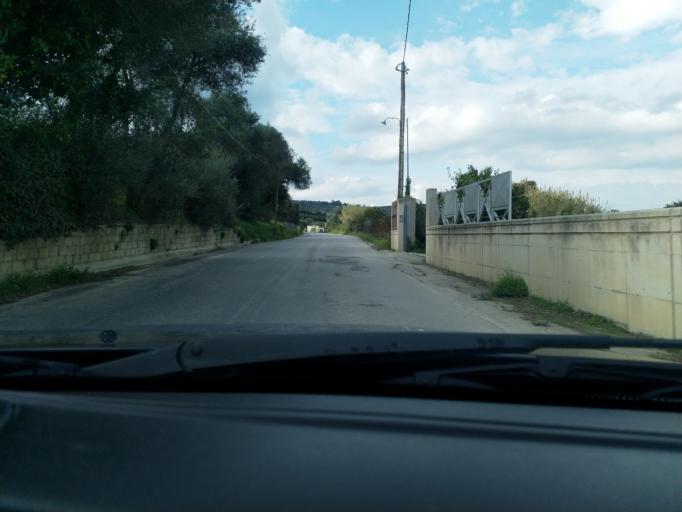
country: GR
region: Crete
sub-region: Nomos Chanias
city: Gerani
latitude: 35.4994
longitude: 23.8998
